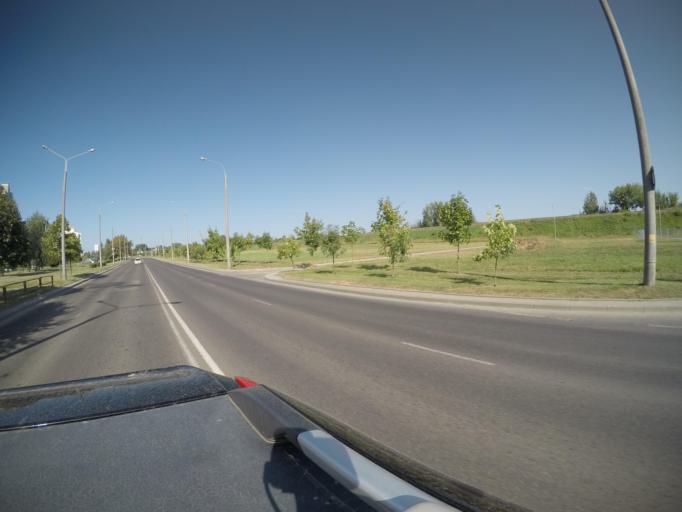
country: BY
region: Grodnenskaya
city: Hrodna
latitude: 53.7153
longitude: 23.8570
